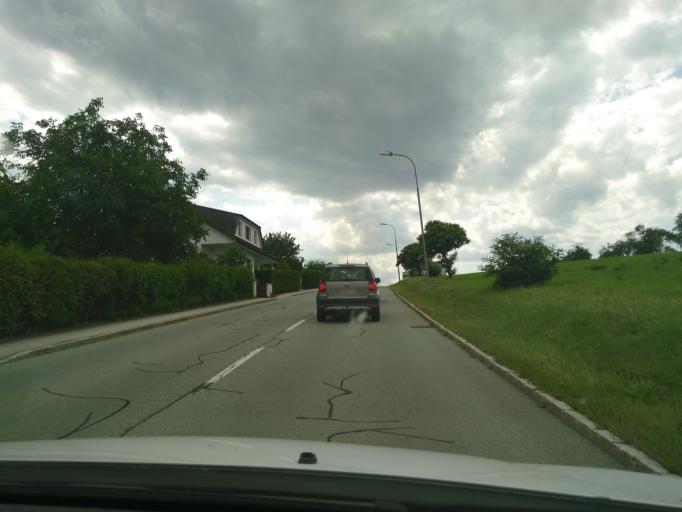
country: AT
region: Burgenland
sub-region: Politischer Bezirk Oberwart
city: Oberschutzen
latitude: 47.3498
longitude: 16.2019
